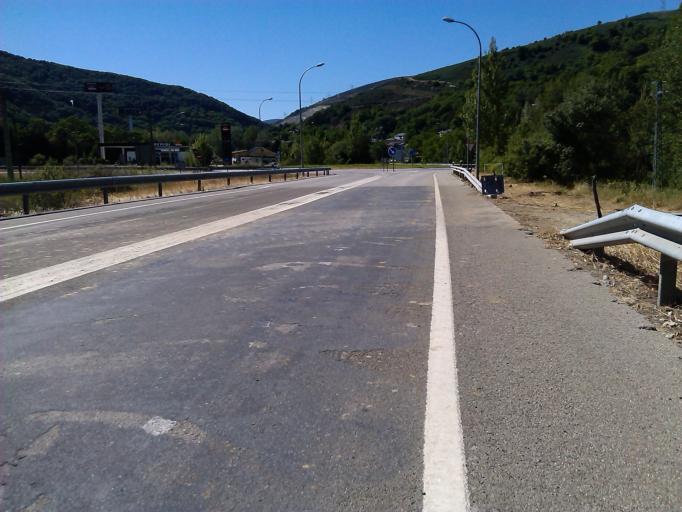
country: ES
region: Castille and Leon
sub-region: Provincia de Leon
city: Trabadelo
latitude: 42.6457
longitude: -6.8744
